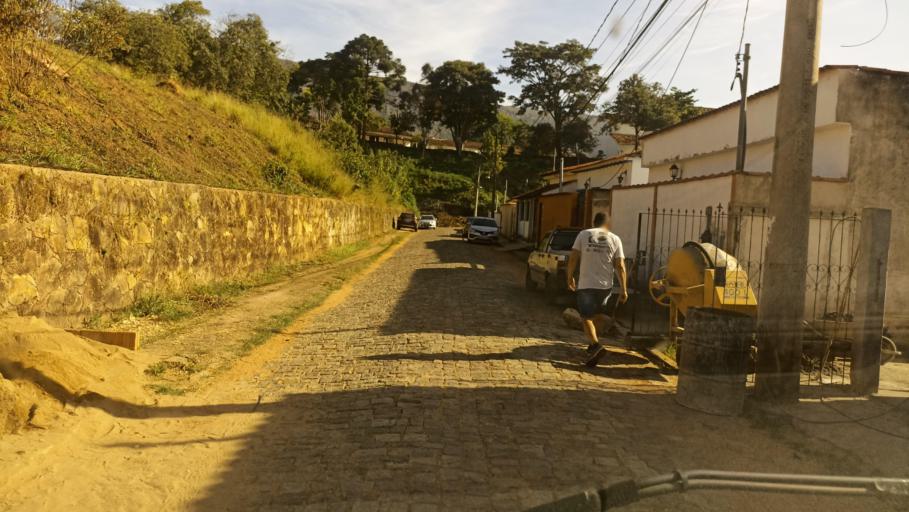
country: BR
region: Minas Gerais
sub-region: Tiradentes
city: Tiradentes
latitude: -21.1142
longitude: -44.1833
